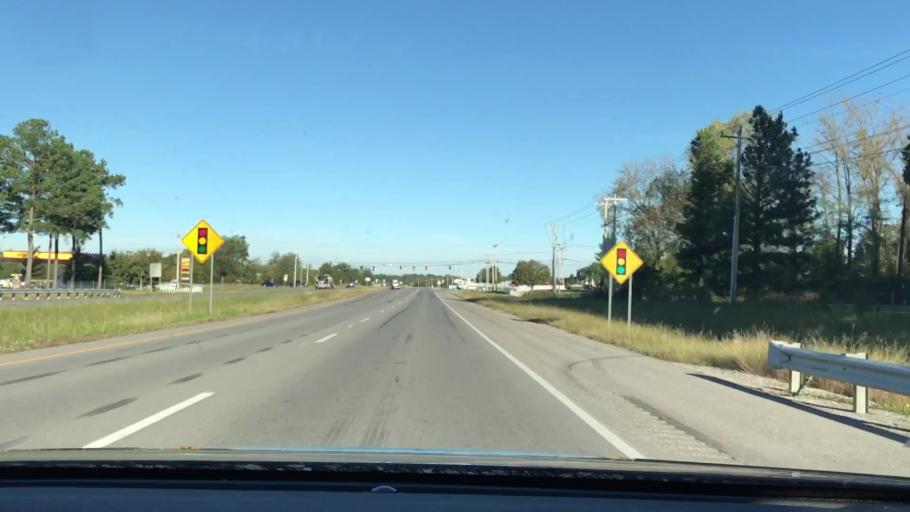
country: US
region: Kentucky
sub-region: Christian County
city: Hopkinsville
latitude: 36.8203
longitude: -87.5026
